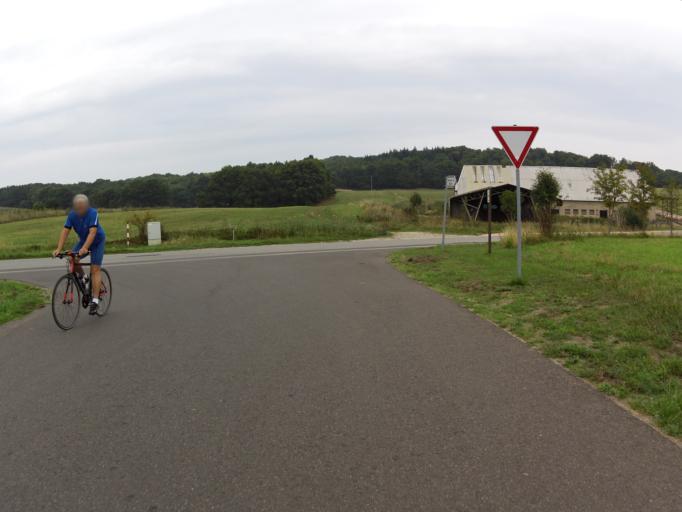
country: PL
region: West Pomeranian Voivodeship
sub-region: Swinoujscie
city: Swinoujscie
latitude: 53.8789
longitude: 14.2037
